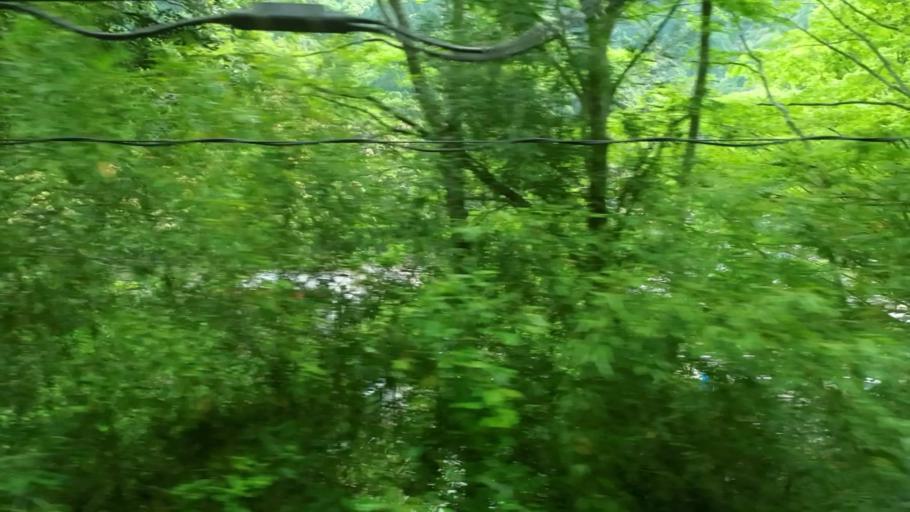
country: JP
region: Tokushima
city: Ikedacho
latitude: 33.9146
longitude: 133.7568
